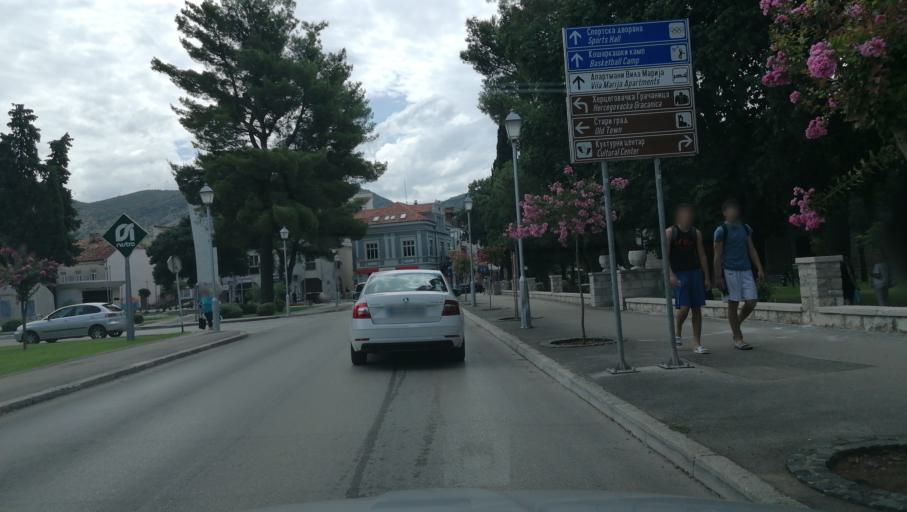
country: BA
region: Republika Srpska
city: Trebinje
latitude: 42.7102
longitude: 18.3457
